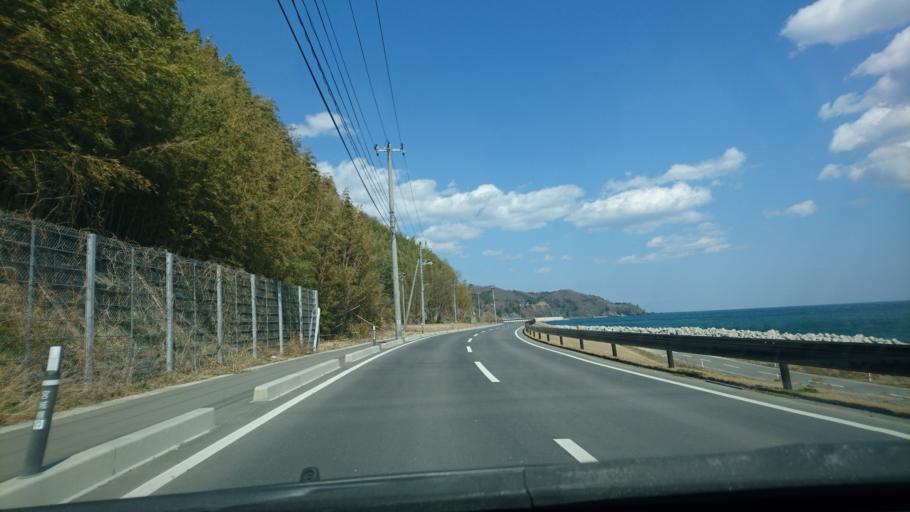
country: JP
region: Miyagi
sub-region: Oshika Gun
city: Onagawa Cho
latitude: 38.5773
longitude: 141.4552
